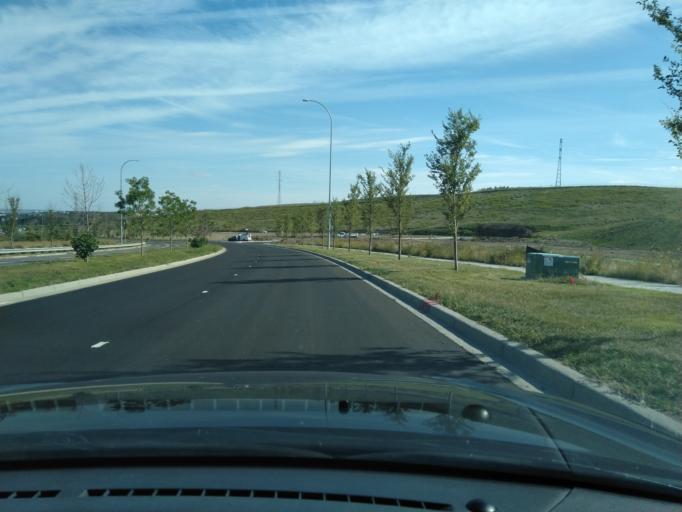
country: CA
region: Alberta
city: Calgary
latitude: 51.1725
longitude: -114.1754
